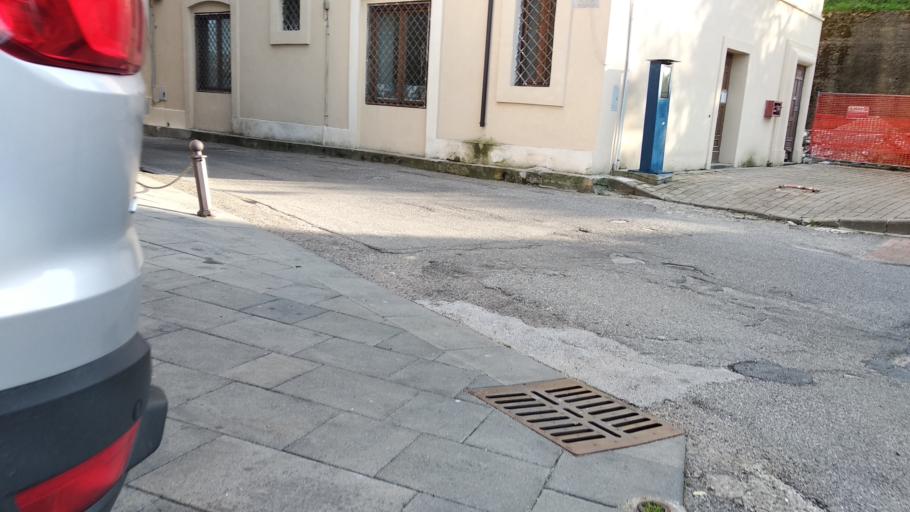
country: IT
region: Calabria
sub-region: Provincia di Cosenza
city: San Marco Argentano
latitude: 39.5581
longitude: 16.1196
